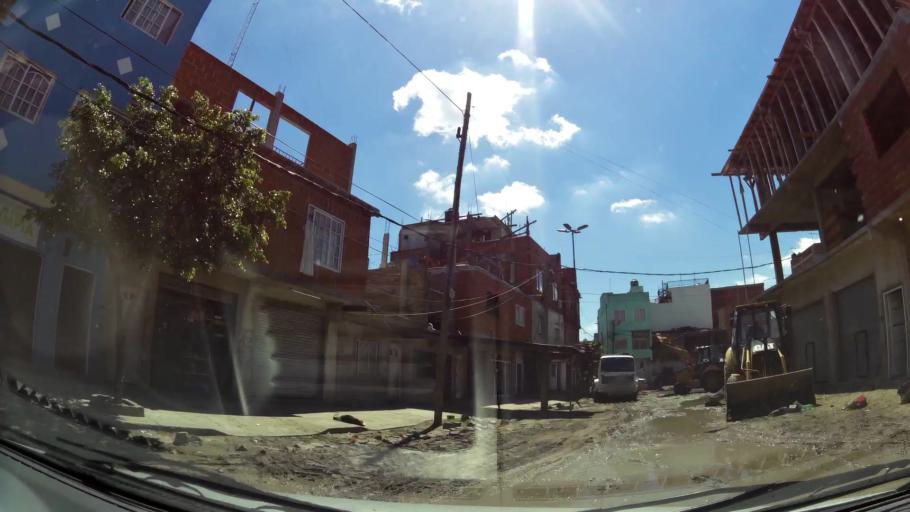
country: AR
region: Buenos Aires
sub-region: Partido de Lanus
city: Lanus
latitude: -34.6601
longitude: -58.4156
